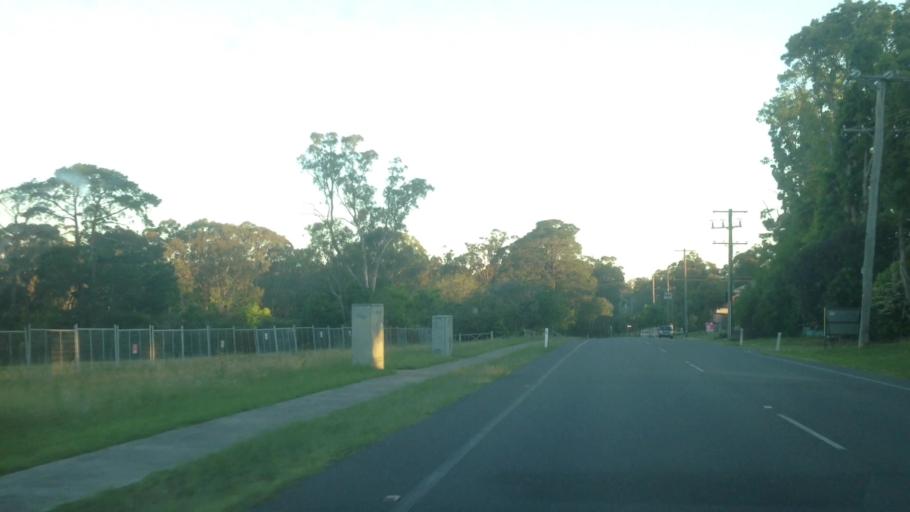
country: AU
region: New South Wales
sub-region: Lake Macquarie Shire
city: Dora Creek
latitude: -33.1030
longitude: 151.4788
